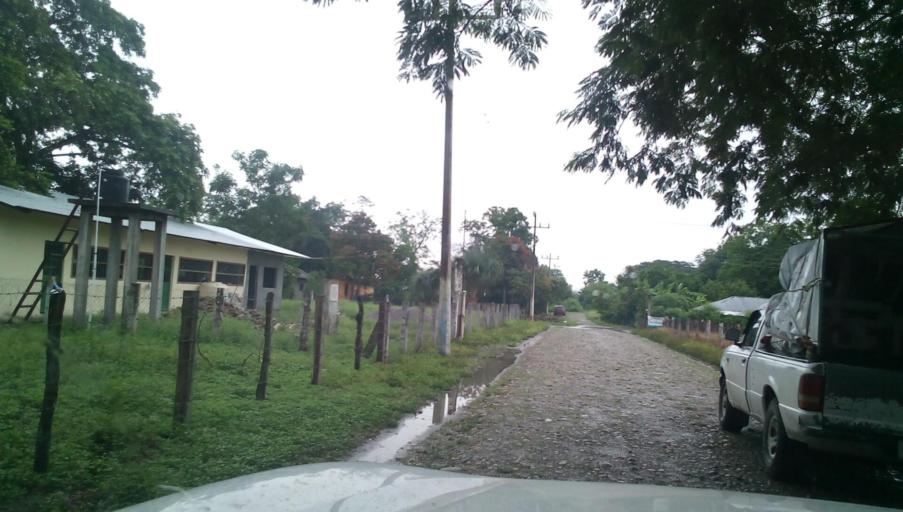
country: MX
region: Veracruz
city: Tempoal de Sanchez
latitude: 21.4173
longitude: -98.4245
